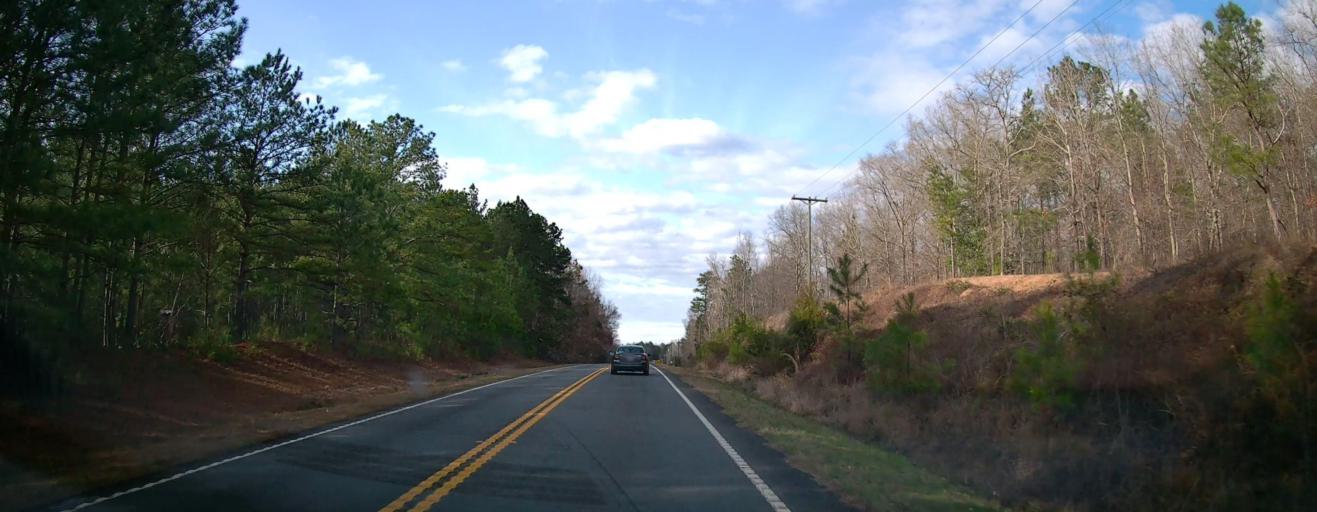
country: US
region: Georgia
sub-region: Talbot County
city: Talbotton
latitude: 32.5464
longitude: -84.6018
